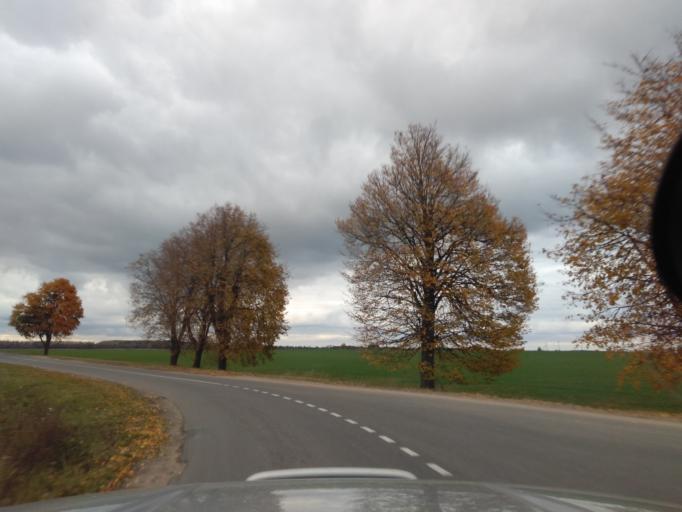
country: BY
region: Minsk
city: Slutsk
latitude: 53.2064
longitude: 27.3672
